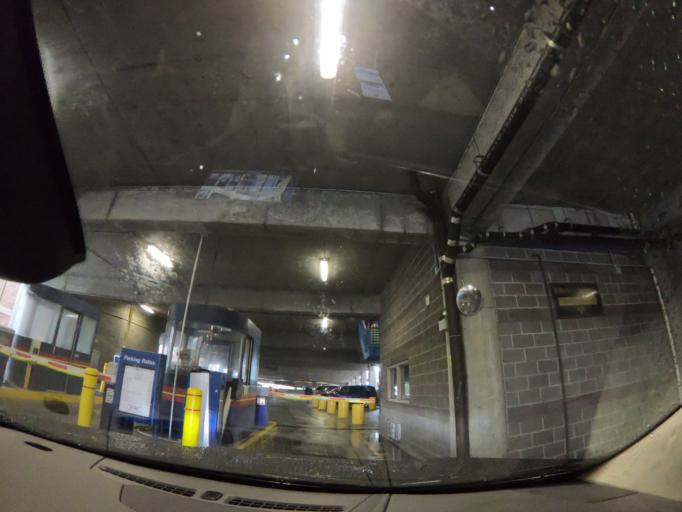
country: US
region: Kentucky
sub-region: Jefferson County
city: Louisville
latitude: 38.2567
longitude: -85.7639
